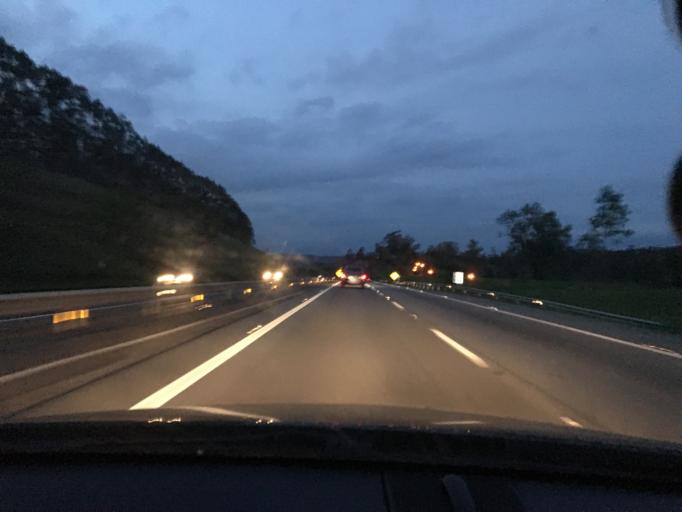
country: BR
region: Sao Paulo
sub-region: Santa Isabel
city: Santa Isabel
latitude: -23.3571
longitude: -46.1259
